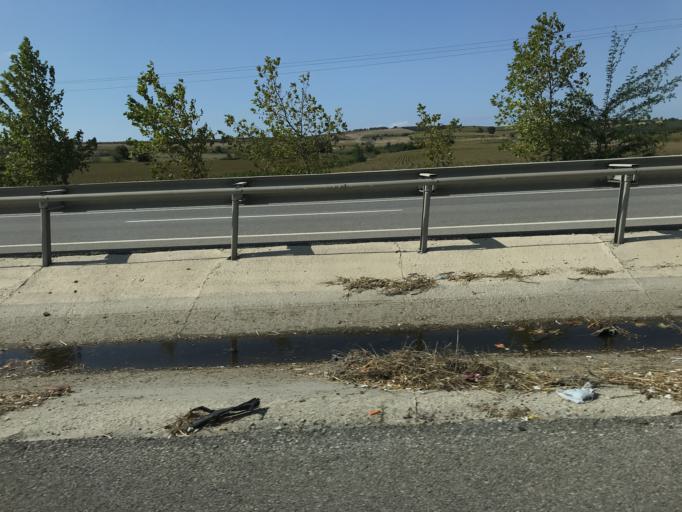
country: TR
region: Bursa
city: Mahmudiye
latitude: 40.2098
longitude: 28.6056
